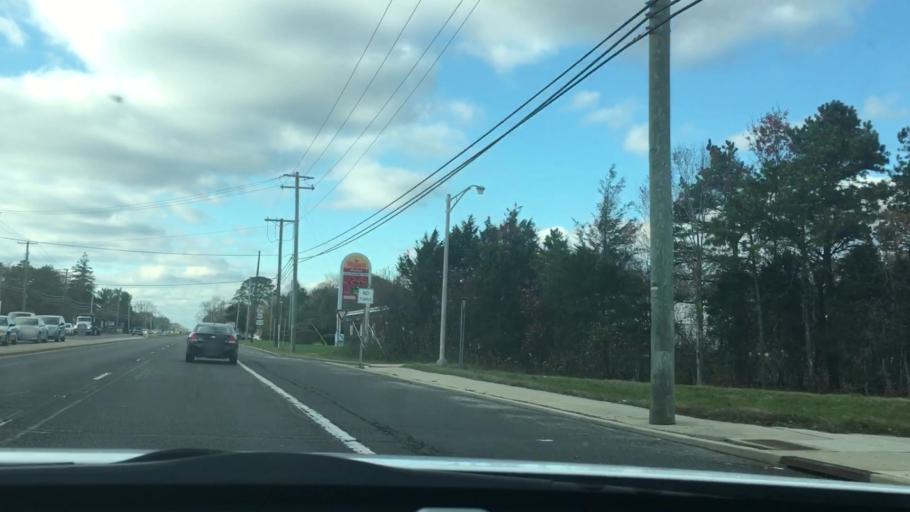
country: US
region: New Jersey
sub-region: Atlantic County
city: Northfield
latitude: 39.4099
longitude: -74.5677
